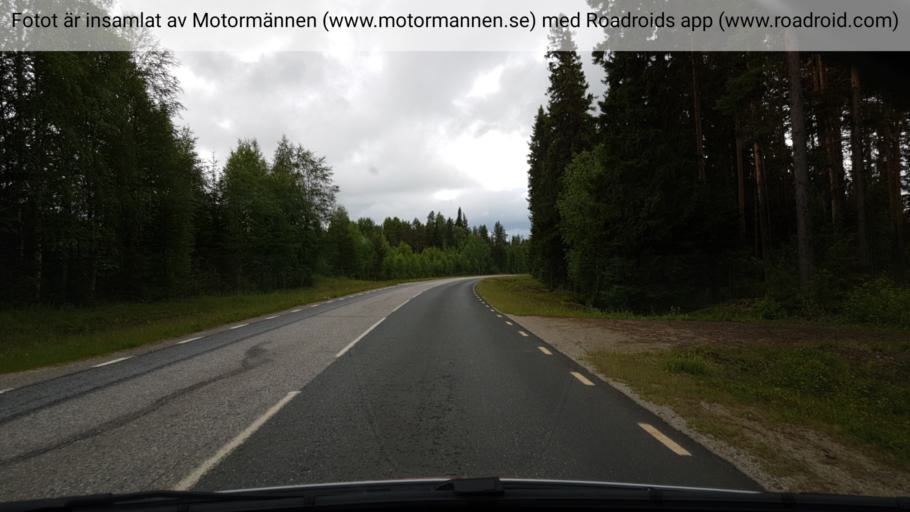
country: SE
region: Vaesterbotten
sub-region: Norsjo Kommun
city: Norsjoe
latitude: 64.6312
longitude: 19.2885
